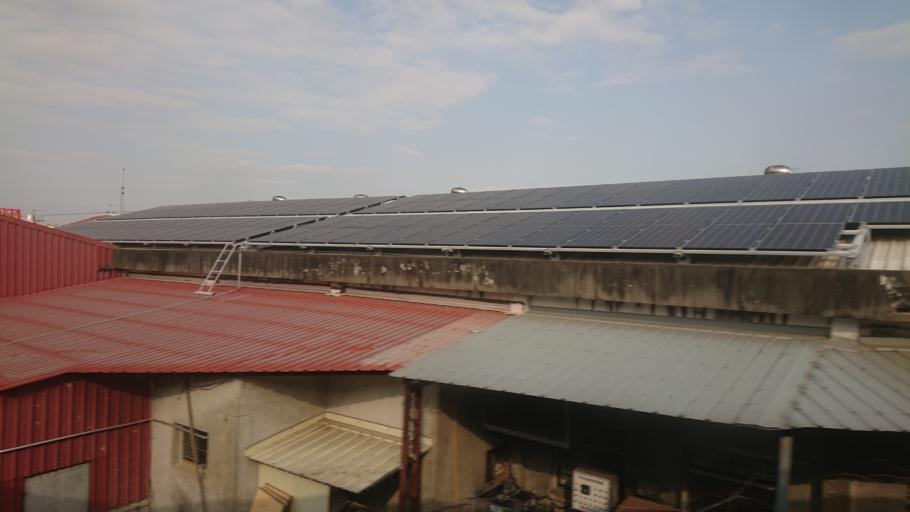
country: TW
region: Taiwan
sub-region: Yunlin
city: Douliu
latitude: 23.6798
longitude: 120.4868
